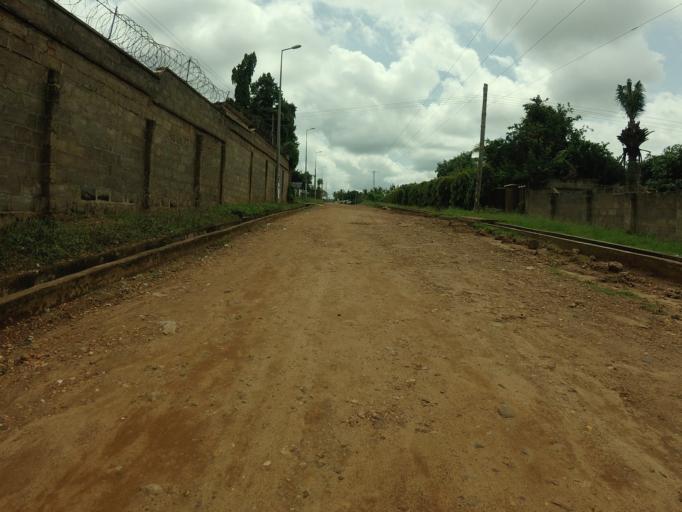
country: GH
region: Volta
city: Ho
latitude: 6.5940
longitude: 0.4701
